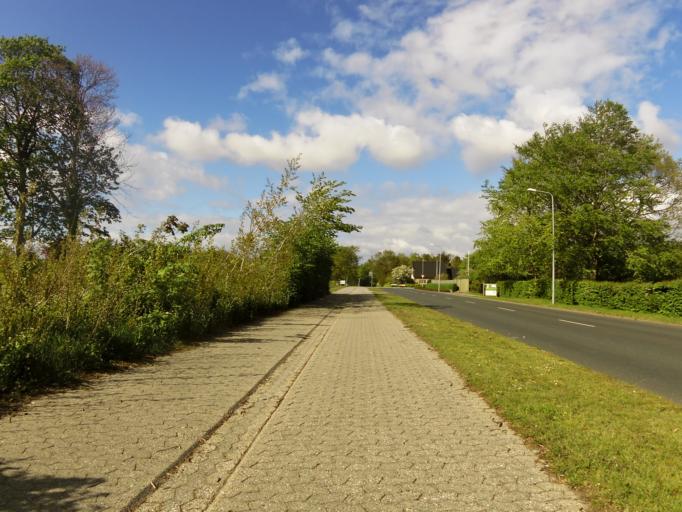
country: DK
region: South Denmark
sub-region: Esbjerg Kommune
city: Ribe
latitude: 55.2828
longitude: 8.7256
